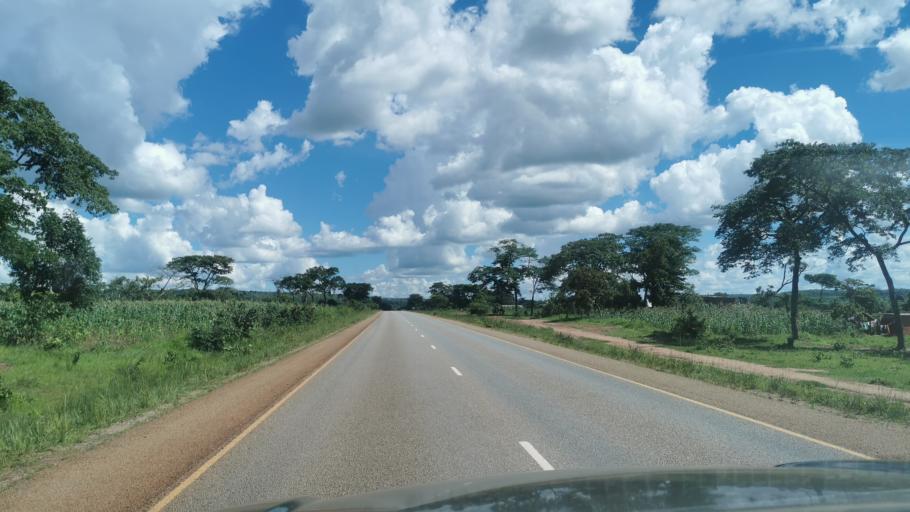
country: TZ
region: Geita
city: Uyovu
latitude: -3.0904
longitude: 31.2948
